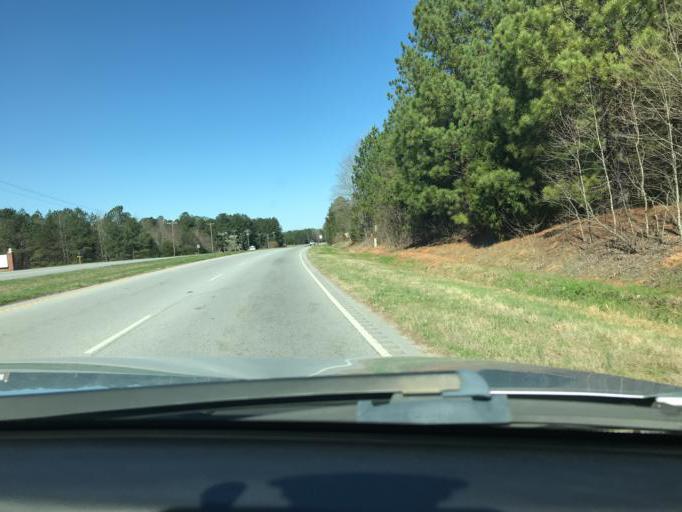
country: US
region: South Carolina
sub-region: Laurens County
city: Watts Mills
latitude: 34.4809
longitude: -81.9482
